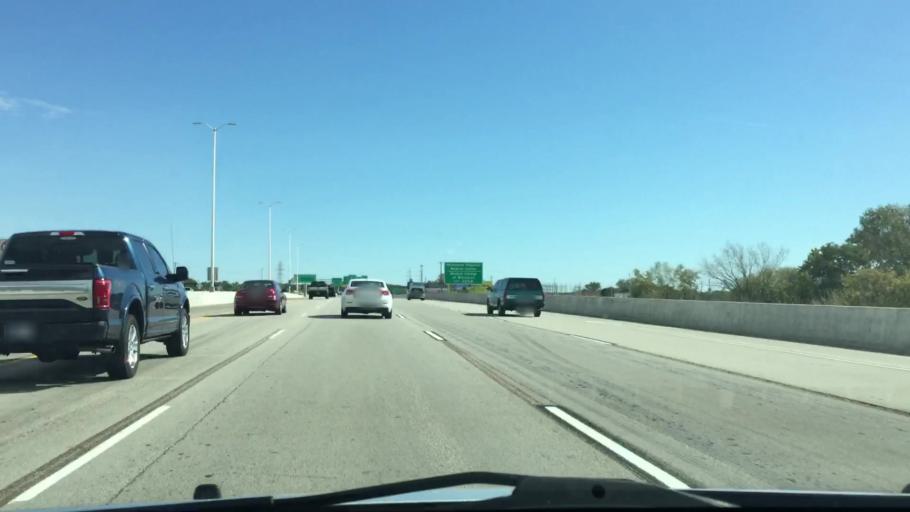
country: US
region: Wisconsin
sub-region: Waukesha County
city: Elm Grove
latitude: 43.0290
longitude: -88.0691
